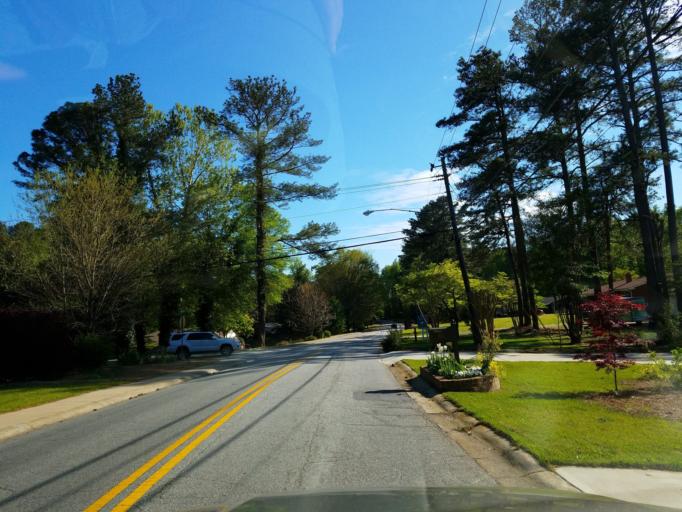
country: US
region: Georgia
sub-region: Cobb County
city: Smyrna
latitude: 33.8577
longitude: -84.5367
